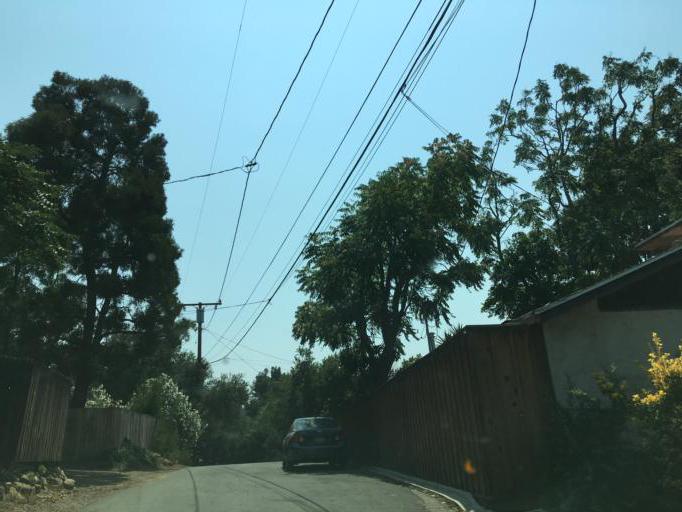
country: US
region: California
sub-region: Los Angeles County
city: Topanga
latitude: 34.1047
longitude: -118.5893
